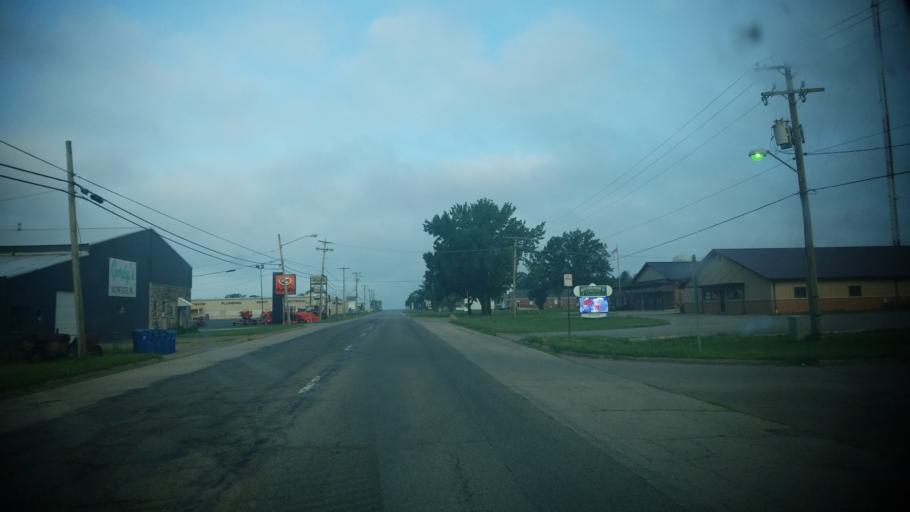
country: US
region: Illinois
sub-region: Wayne County
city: Fairfield
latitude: 38.3797
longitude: -88.3814
